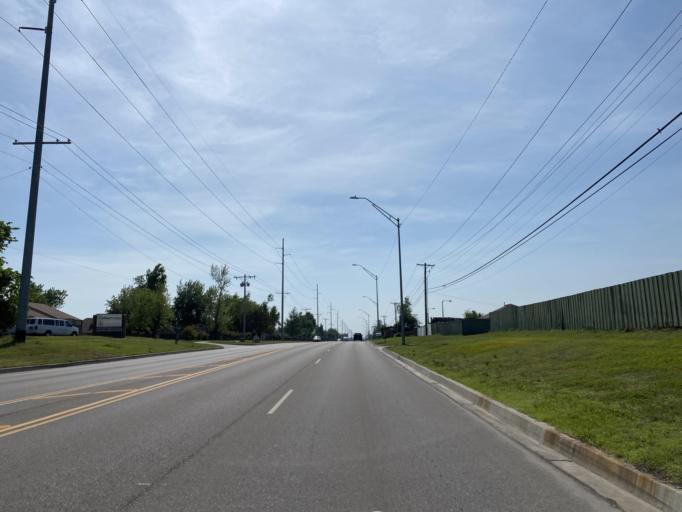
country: US
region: Oklahoma
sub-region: Oklahoma County
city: Nicoma Park
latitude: 35.4499
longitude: -97.3383
